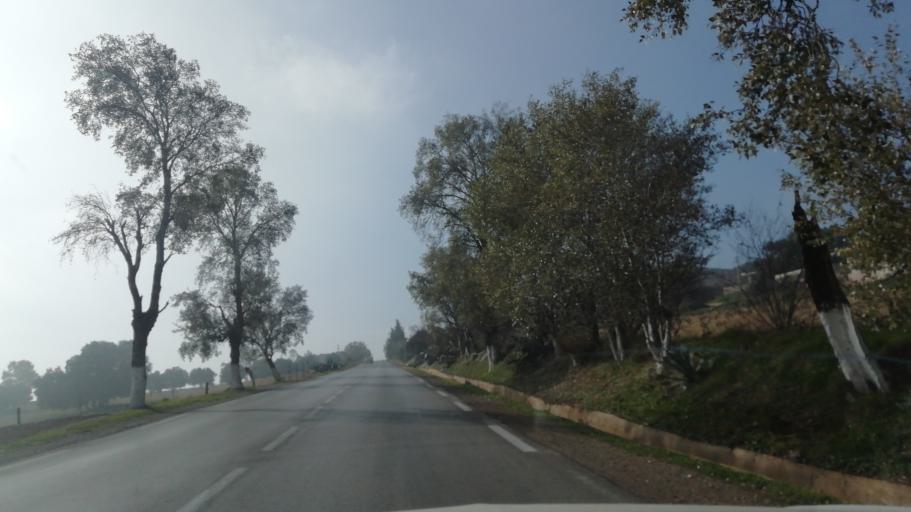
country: DZ
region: Mascara
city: Mascara
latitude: 35.5285
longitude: 0.3537
